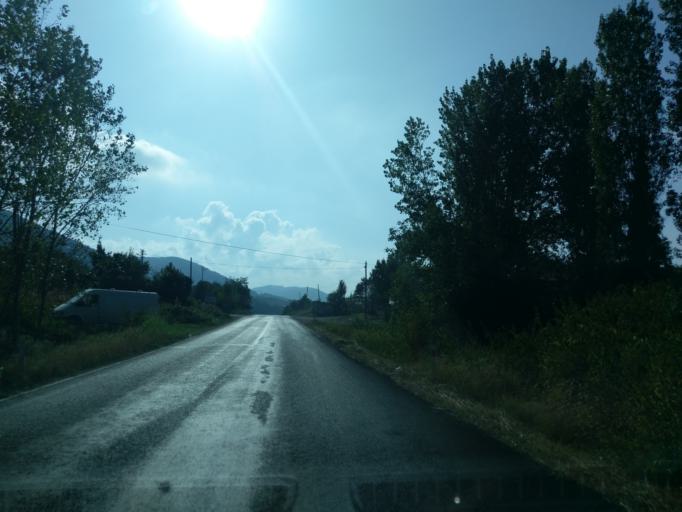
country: TR
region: Sinop
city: Yenikonak
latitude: 41.9426
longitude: 34.7266
